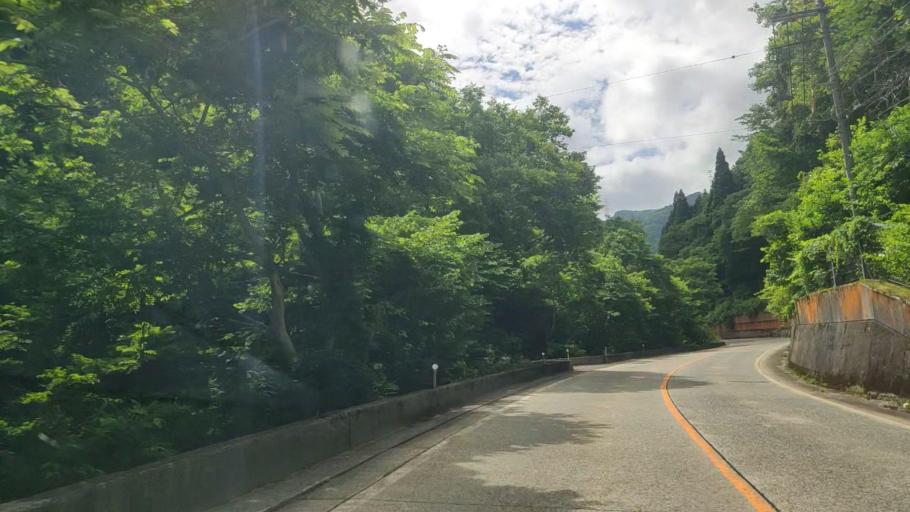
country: JP
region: Okayama
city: Niimi
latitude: 35.2102
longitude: 133.4905
